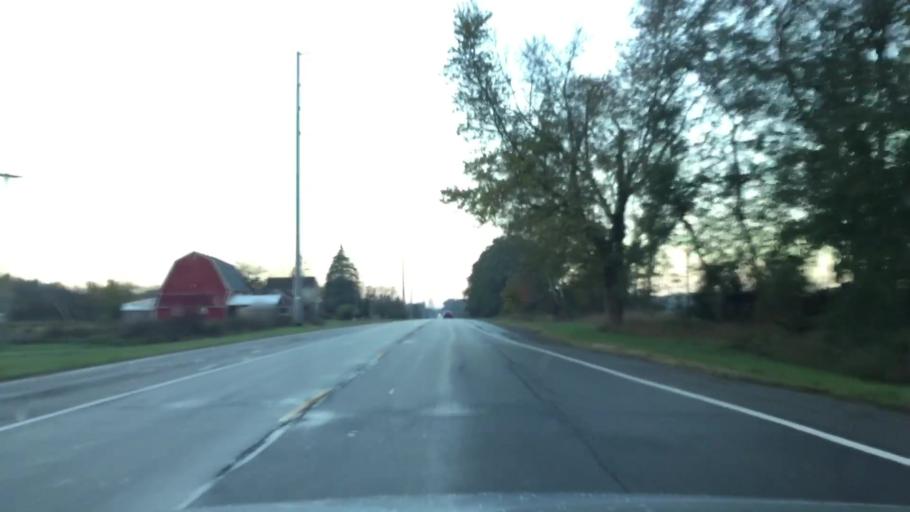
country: US
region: Michigan
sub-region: Livingston County
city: Howell
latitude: 42.6304
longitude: -83.8457
